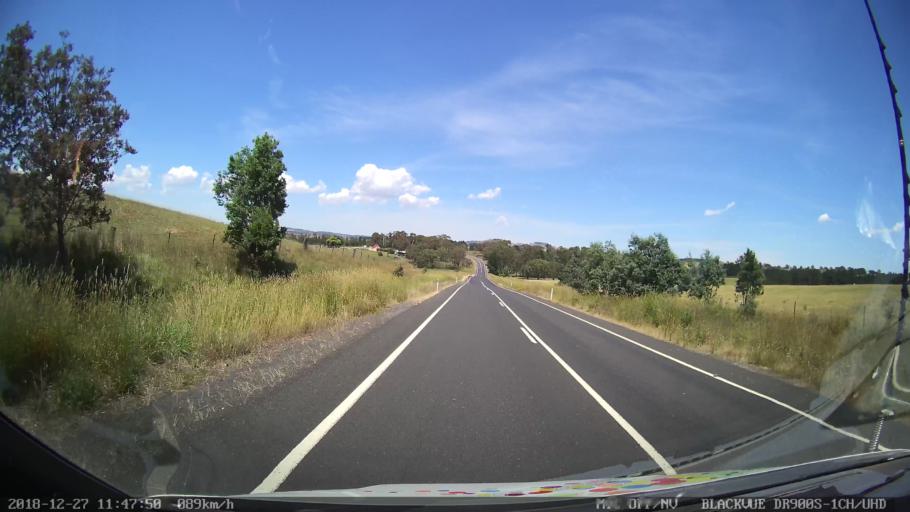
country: AU
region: New South Wales
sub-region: Bathurst Regional
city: Perthville
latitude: -33.5994
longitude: 149.4404
